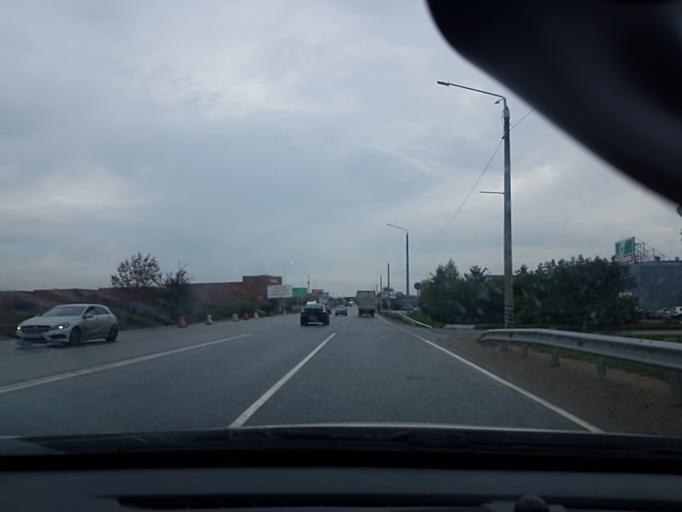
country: RU
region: Moskovskaya
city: Pavlovskaya Sloboda
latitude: 55.8150
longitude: 37.0646
